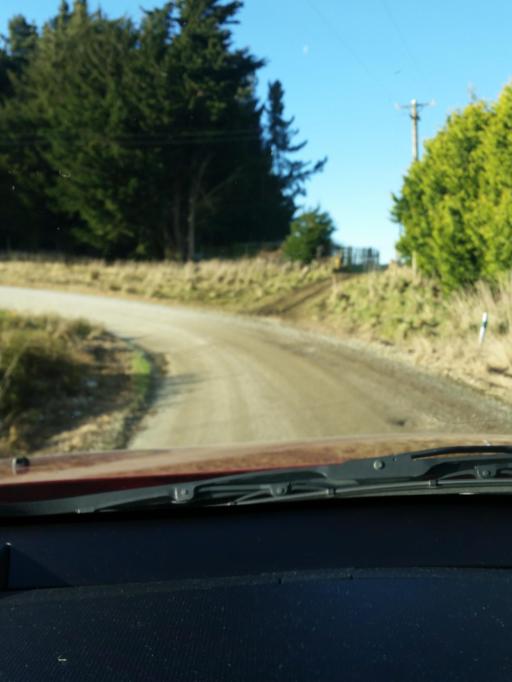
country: NZ
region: Southland
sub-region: Gore District
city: Gore
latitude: -46.2411
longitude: 168.7614
